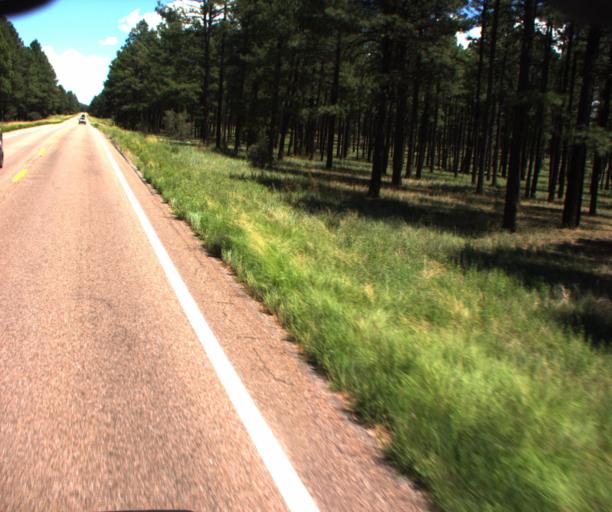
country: US
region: Arizona
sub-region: Navajo County
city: Lake of the Woods
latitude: 34.1216
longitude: -110.1251
